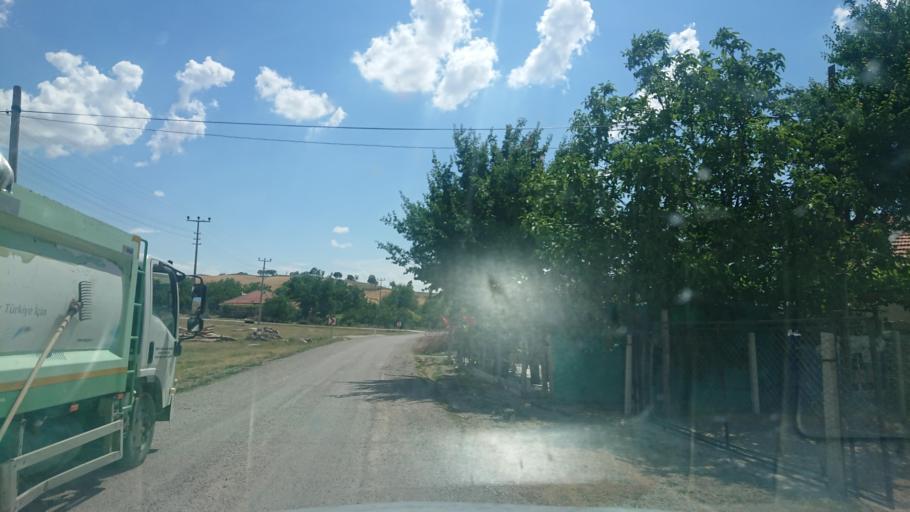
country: TR
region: Aksaray
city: Agacoren
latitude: 38.8380
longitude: 33.8124
